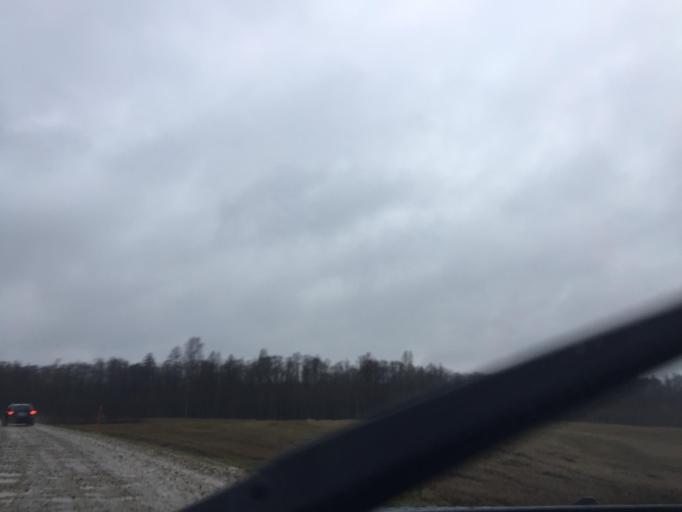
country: LV
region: Salacgrivas
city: Salacgriva
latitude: 57.7718
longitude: 24.5248
